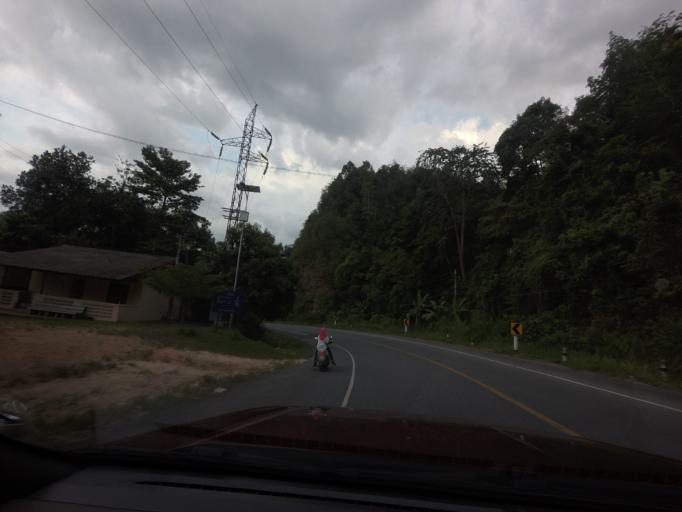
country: TH
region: Yala
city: Than To
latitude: 5.9935
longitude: 101.1928
